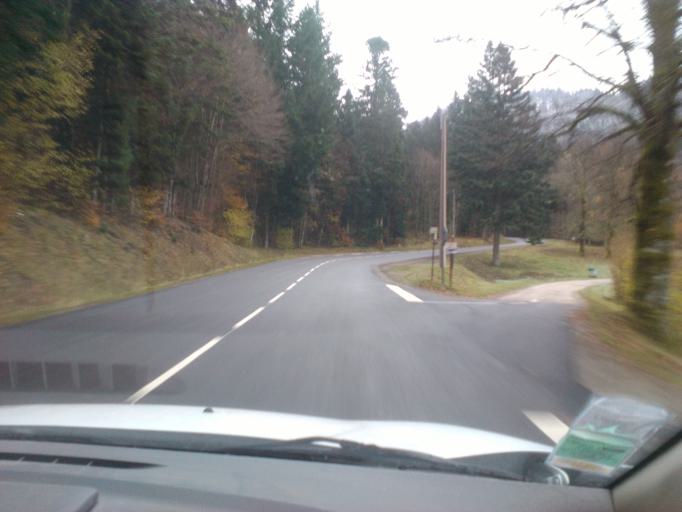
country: FR
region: Lorraine
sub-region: Departement des Vosges
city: Xonrupt-Longemer
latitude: 48.0565
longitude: 6.9870
